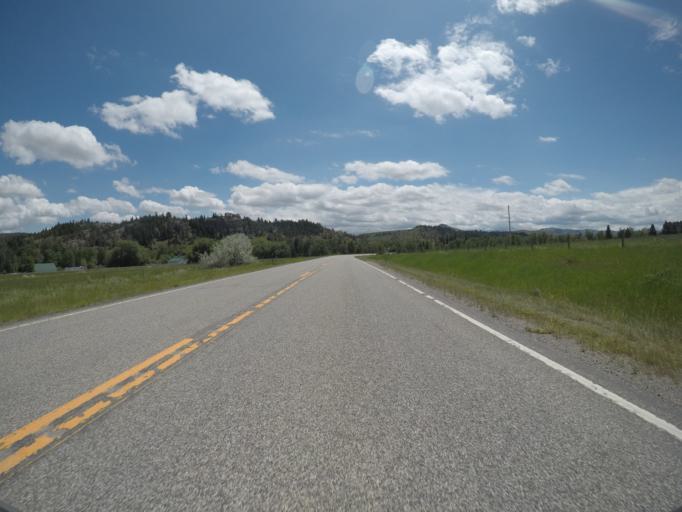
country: US
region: Montana
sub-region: Sweet Grass County
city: Big Timber
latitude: 45.7263
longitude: -109.9975
